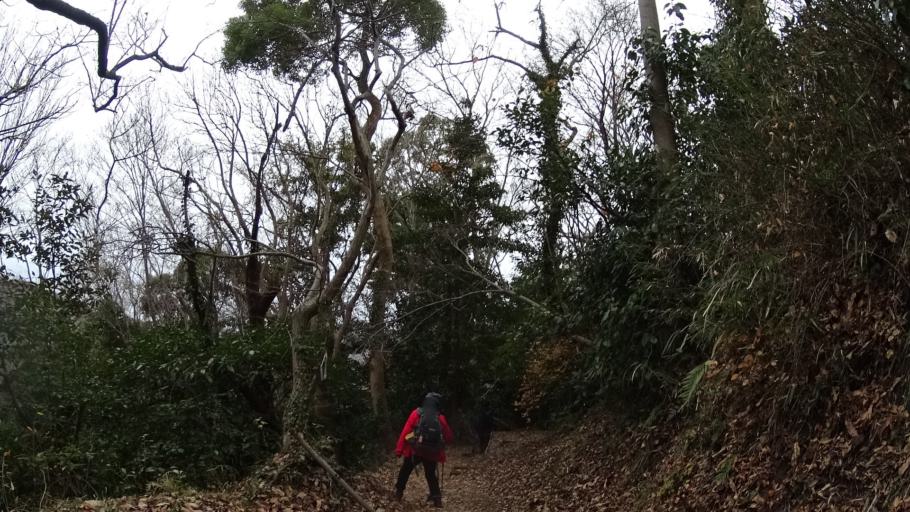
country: JP
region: Kanagawa
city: Oiso
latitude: 35.3188
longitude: 139.3086
